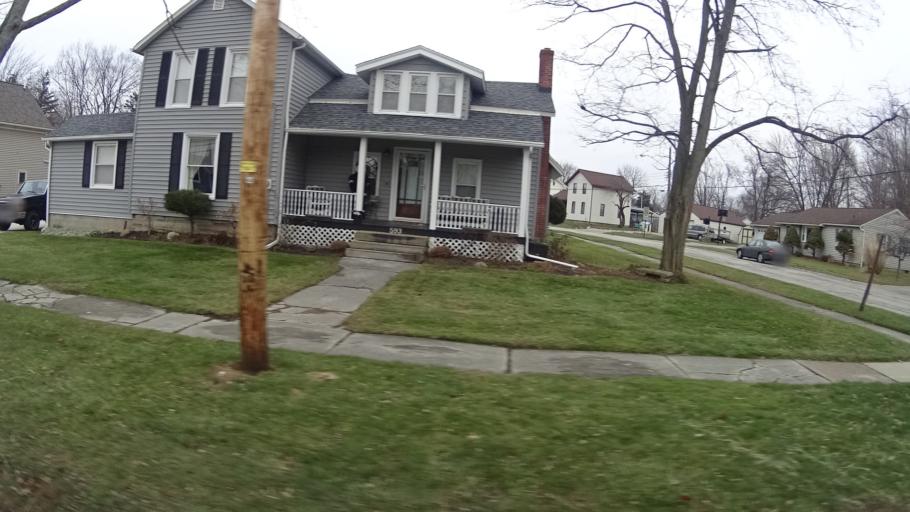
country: US
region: Ohio
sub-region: Lorain County
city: Amherst
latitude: 41.3915
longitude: -82.2214
